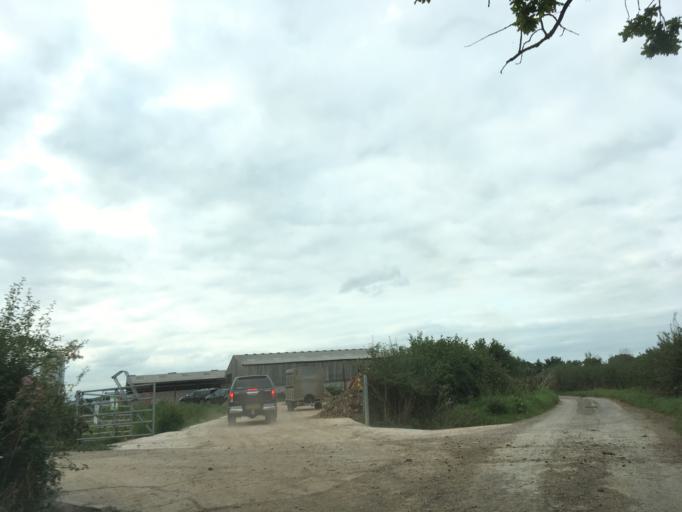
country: GB
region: England
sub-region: South Gloucestershire
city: Falfield
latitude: 51.6456
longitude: -2.4667
